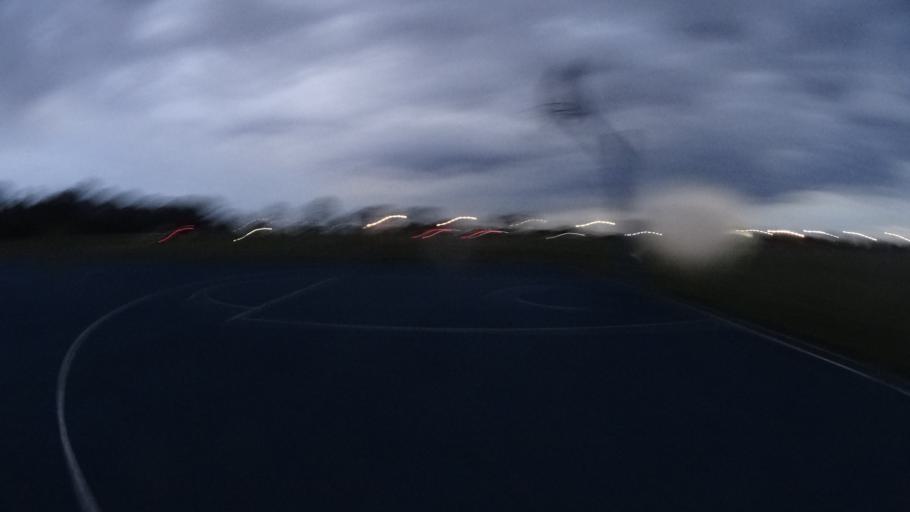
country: PL
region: Masovian Voivodeship
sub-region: Powiat warszawski zachodni
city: Ozarow Mazowiecki
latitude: 52.2332
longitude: 20.7997
